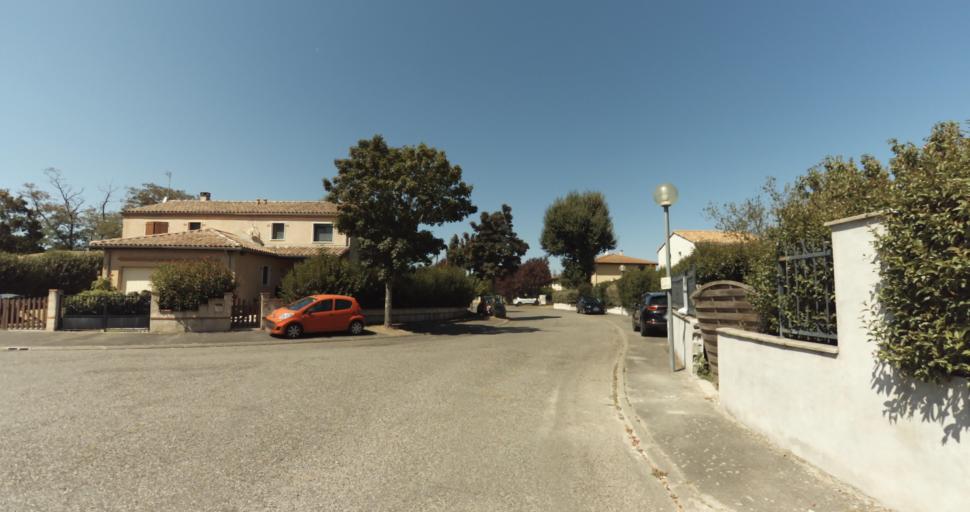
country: FR
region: Midi-Pyrenees
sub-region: Departement de la Haute-Garonne
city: L'Union
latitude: 43.6487
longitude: 1.4900
